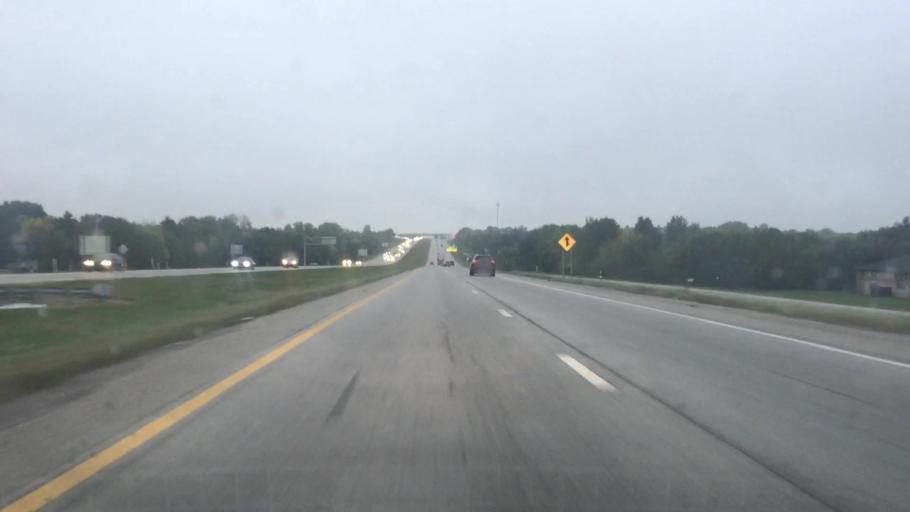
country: US
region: Kansas
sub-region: Johnson County
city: Lenexa
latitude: 38.8539
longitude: -94.6774
